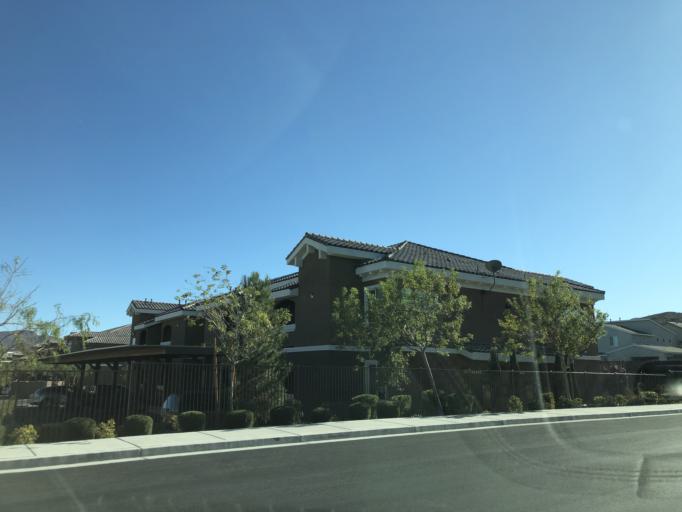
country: US
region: Nevada
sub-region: Clark County
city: Whitney
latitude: 36.0009
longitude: -115.0876
